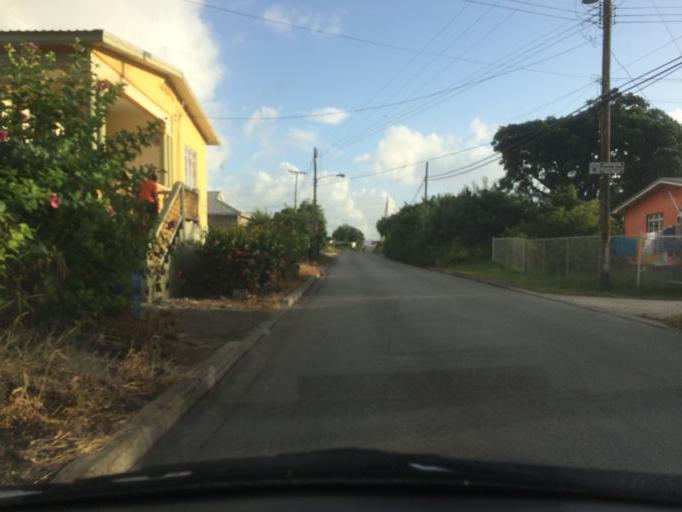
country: BB
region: Saint Lucy
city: Checker Hall
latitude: 13.2878
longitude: -59.6403
